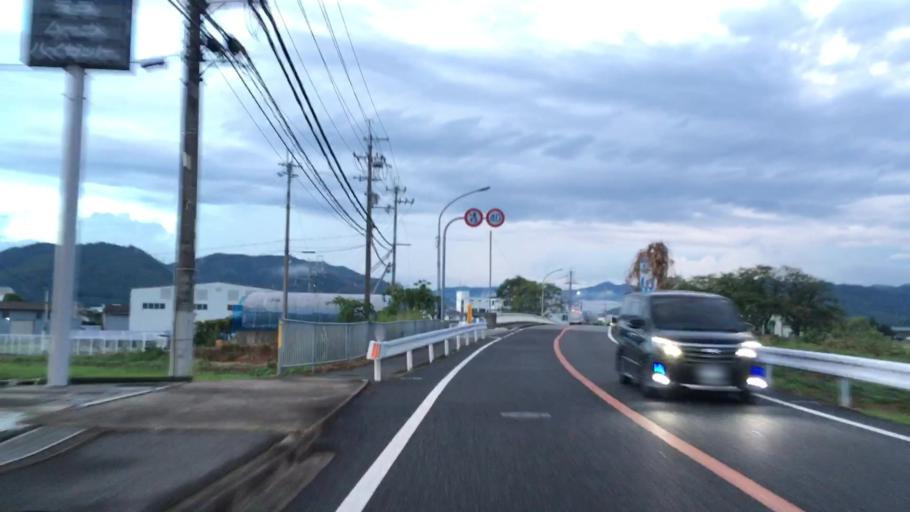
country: JP
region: Hyogo
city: Himeji
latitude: 34.9468
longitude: 134.7479
